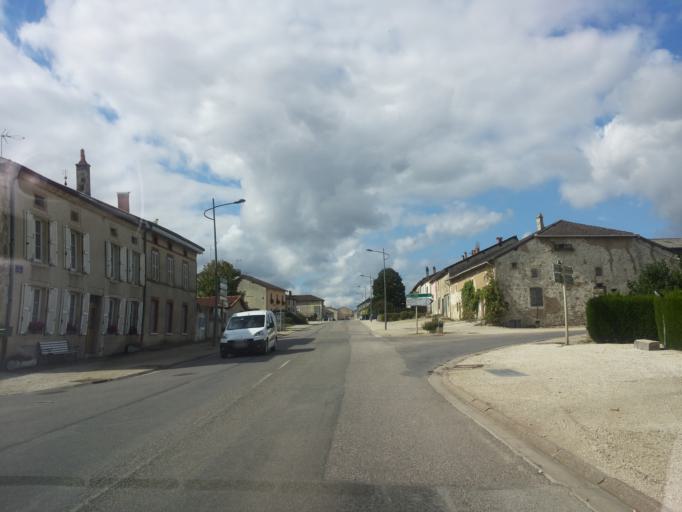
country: FR
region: Lorraine
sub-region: Departement de la Meuse
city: Gondrecourt-le-Chateau
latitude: 48.5499
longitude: 5.4769
